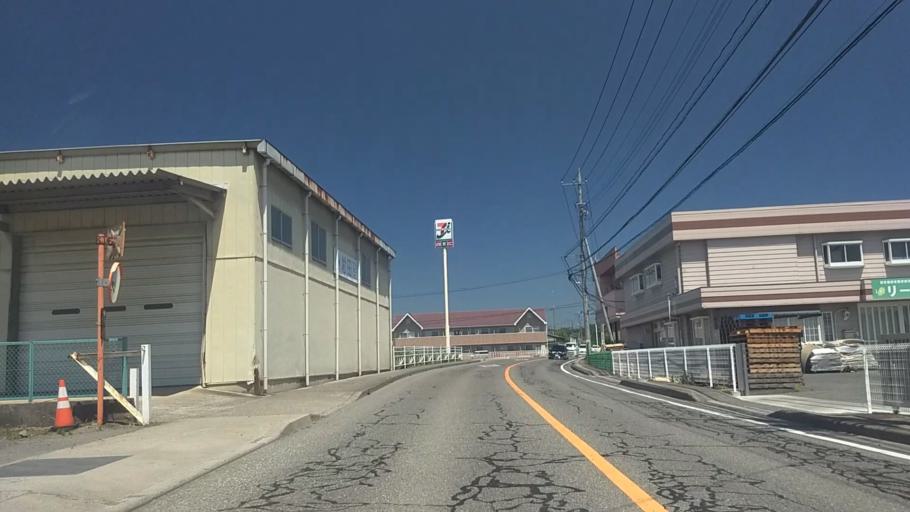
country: JP
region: Yamanashi
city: Nirasaki
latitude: 35.6951
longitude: 138.4570
